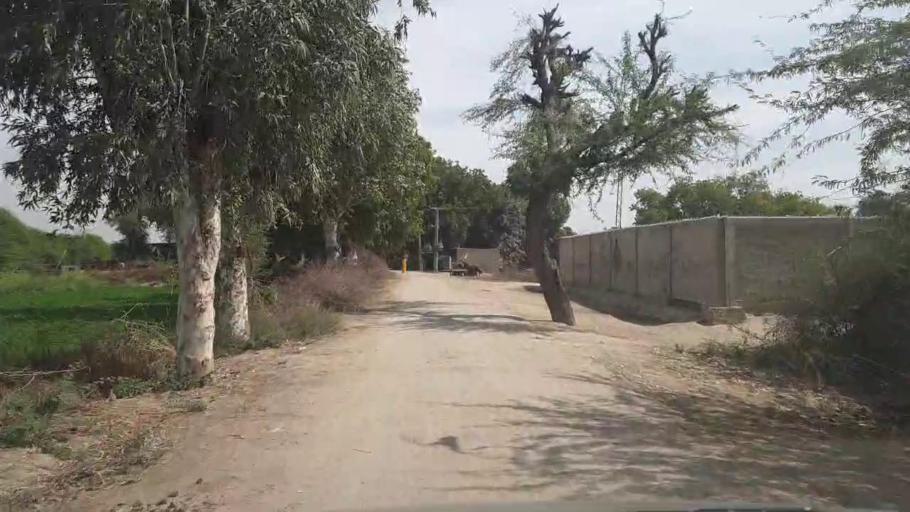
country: PK
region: Sindh
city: Kunri
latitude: 25.2169
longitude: 69.6871
